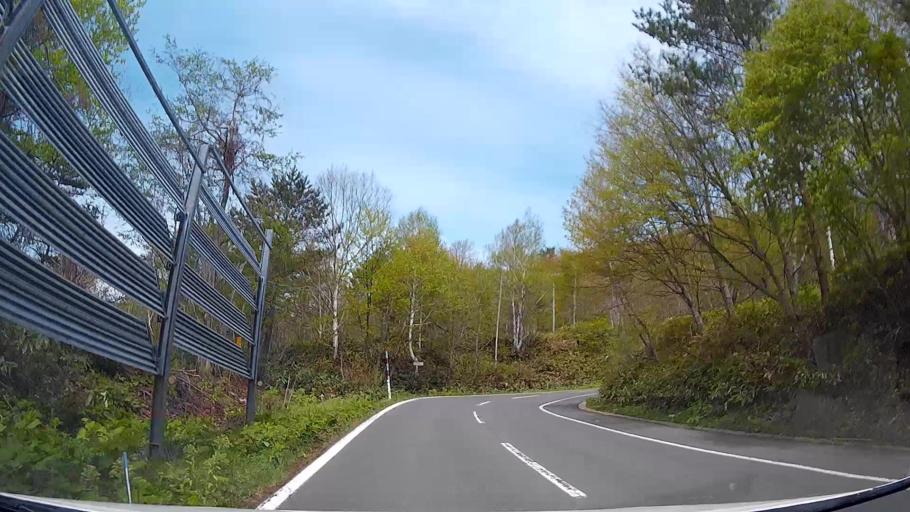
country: JP
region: Iwate
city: Shizukuishi
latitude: 39.9241
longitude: 140.9675
